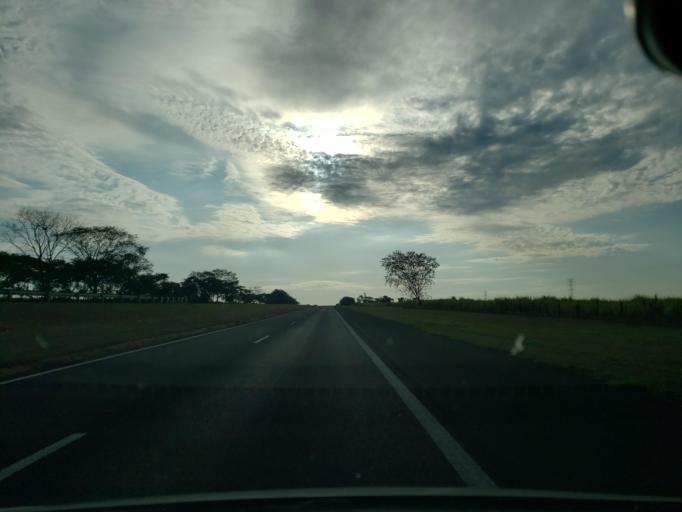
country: BR
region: Sao Paulo
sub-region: Mirandopolis
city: Mirandopolis
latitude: -21.0965
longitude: -51.0464
